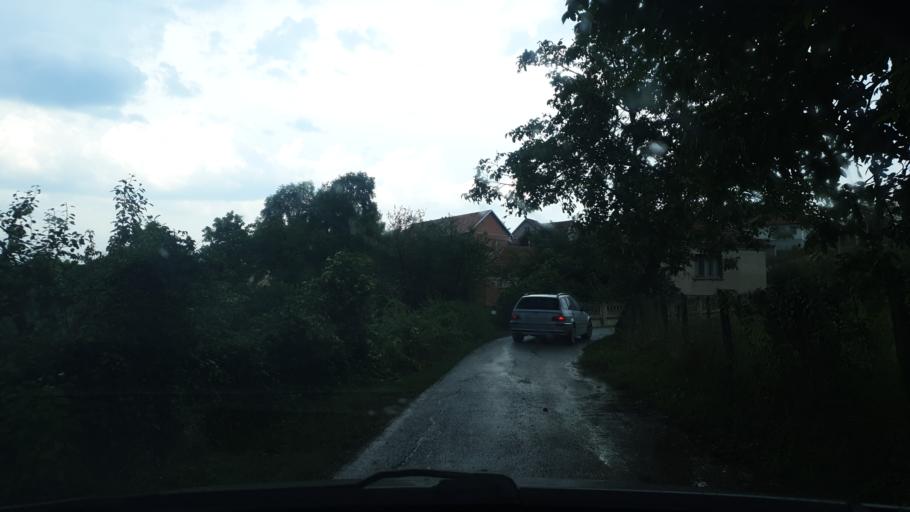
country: RS
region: Central Serbia
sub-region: Sumadijski Okrug
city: Kragujevac
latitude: 44.0808
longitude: 20.7975
